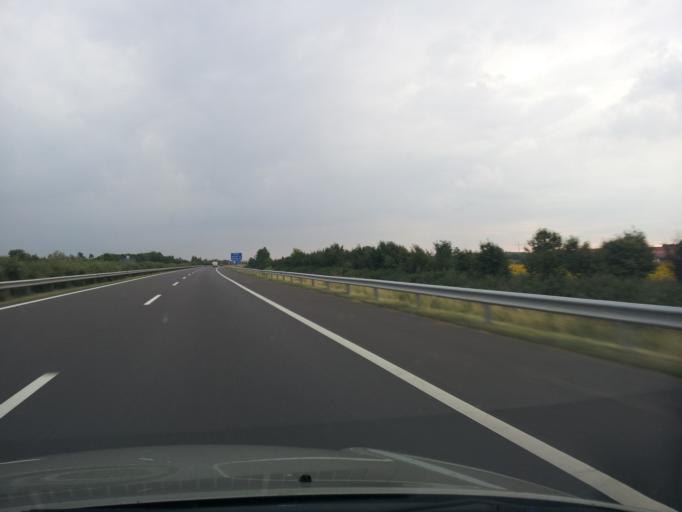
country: HU
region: Borsod-Abauj-Zemplen
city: Mezokeresztes
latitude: 47.8108
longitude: 20.7073
